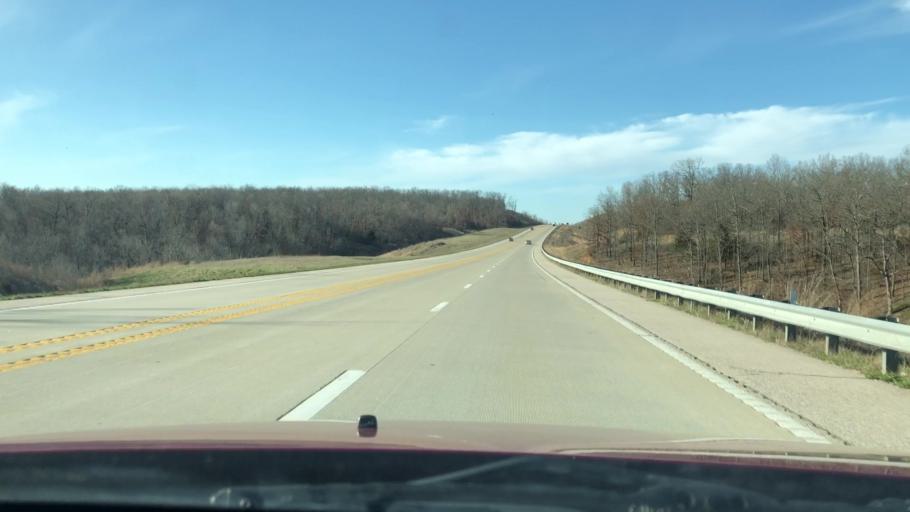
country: US
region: Missouri
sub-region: Camden County
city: Camdenton
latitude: 37.9283
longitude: -92.7130
